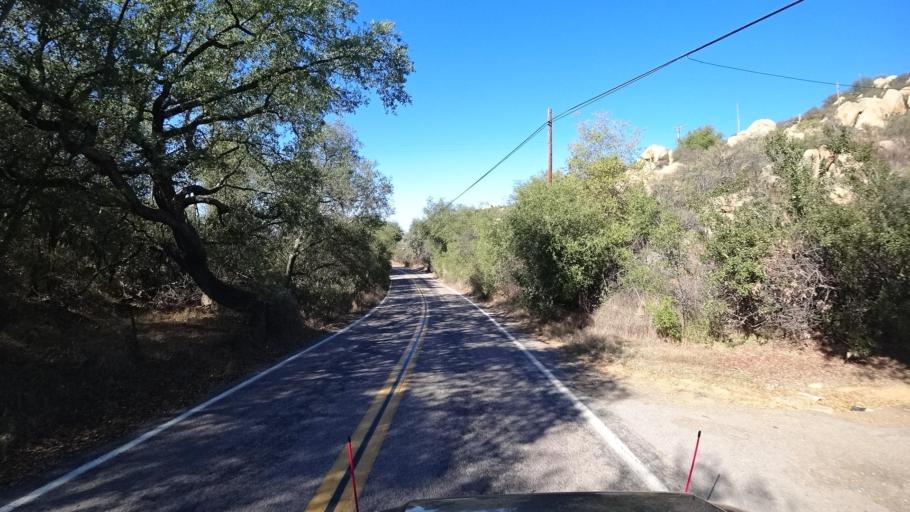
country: US
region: California
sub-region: San Diego County
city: Jamul
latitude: 32.7139
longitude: -116.7731
